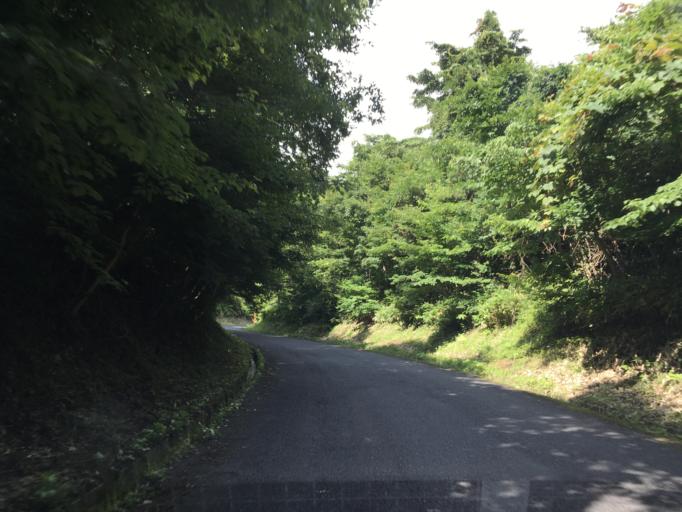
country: JP
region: Iwate
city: Ofunato
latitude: 38.9785
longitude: 141.4345
